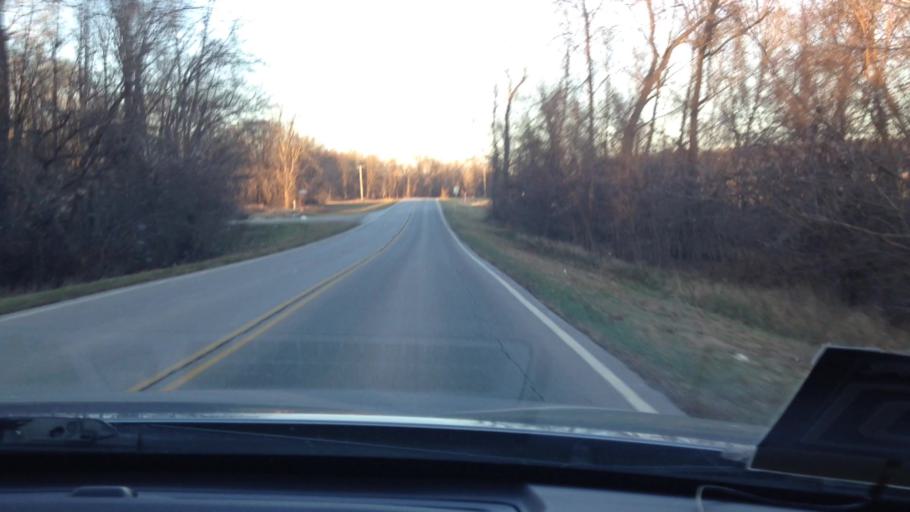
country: US
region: Missouri
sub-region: Platte County
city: Platte City
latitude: 39.3364
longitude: -94.8142
